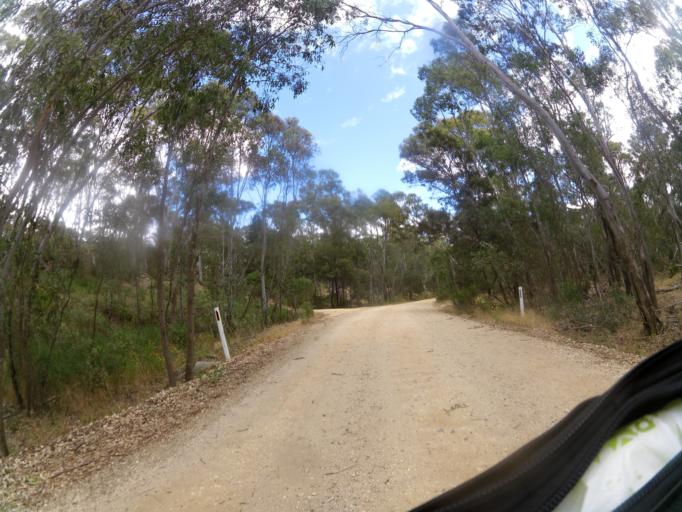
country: AU
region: Victoria
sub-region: Mount Alexander
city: Castlemaine
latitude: -37.0314
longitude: 144.2575
